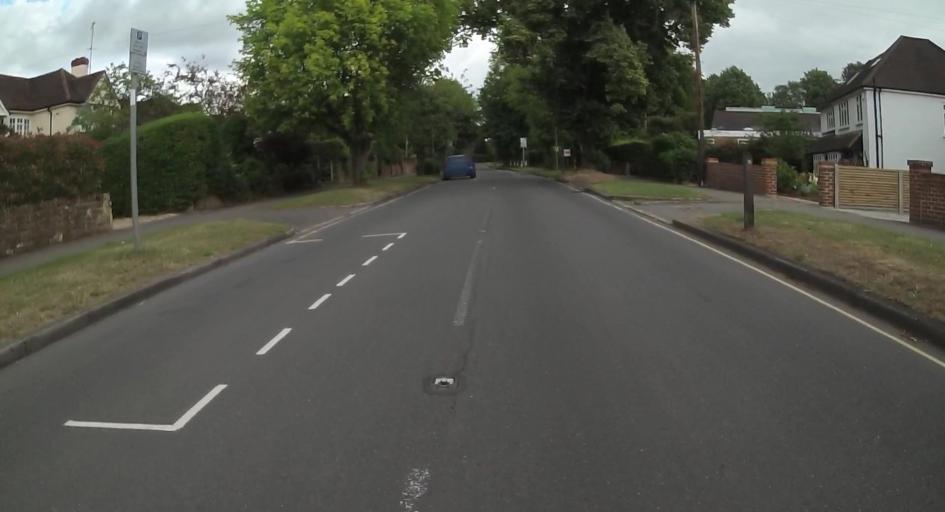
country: GB
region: England
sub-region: Surrey
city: Farnham
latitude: 51.2118
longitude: -0.7892
